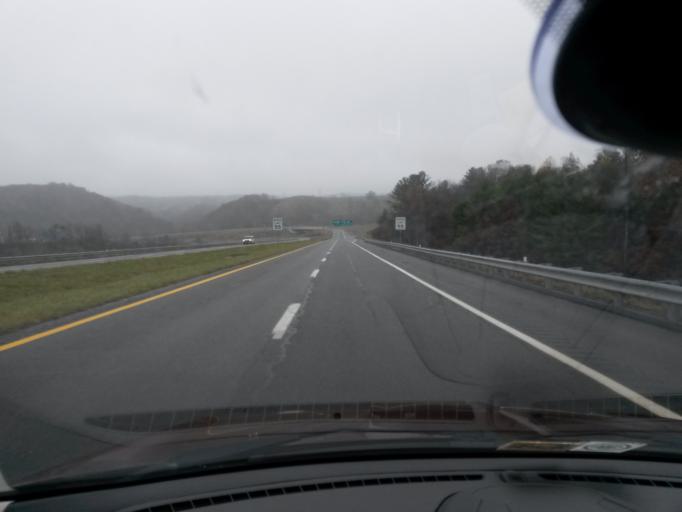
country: US
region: Virginia
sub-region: Carroll County
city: Hillsville
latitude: 36.7476
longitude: -80.7464
